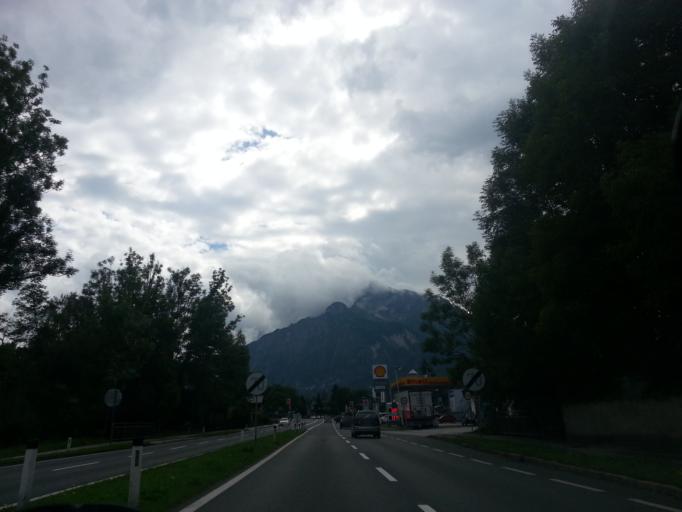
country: AT
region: Salzburg
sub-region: Politischer Bezirk Salzburg-Umgebung
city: Anif
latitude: 47.7494
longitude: 13.0701
